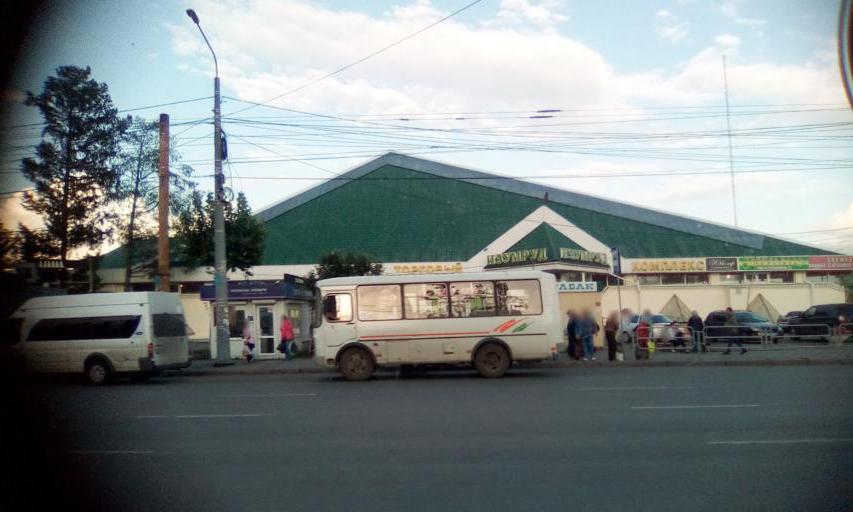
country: RU
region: Chelyabinsk
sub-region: Gorod Chelyabinsk
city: Chelyabinsk
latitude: 55.1376
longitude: 61.3753
